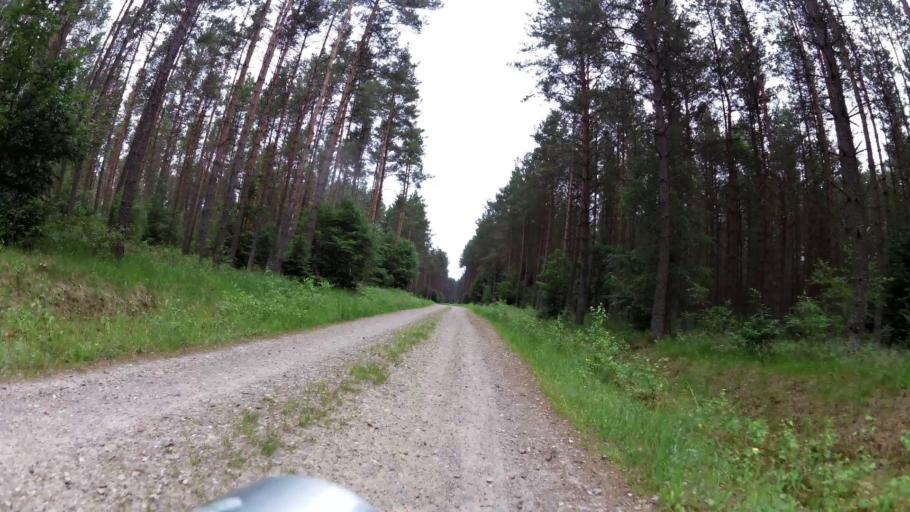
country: PL
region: West Pomeranian Voivodeship
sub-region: Powiat szczecinecki
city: Bialy Bor
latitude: 53.9222
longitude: 16.8353
